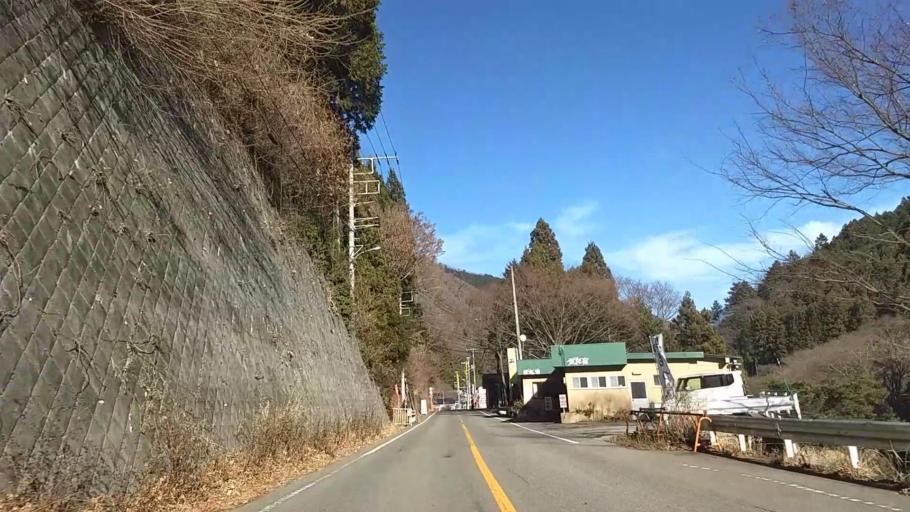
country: JP
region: Yamanashi
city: Otsuki
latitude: 35.5247
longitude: 139.0249
